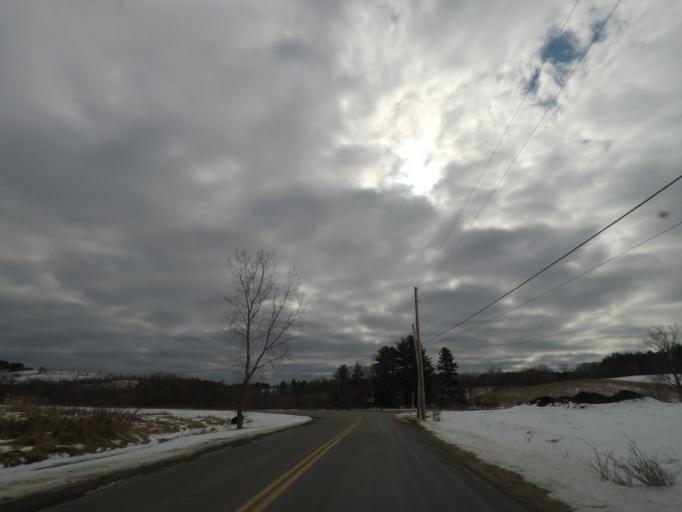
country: US
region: New York
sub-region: Rensselaer County
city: Hoosick Falls
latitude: 42.8759
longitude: -73.4126
